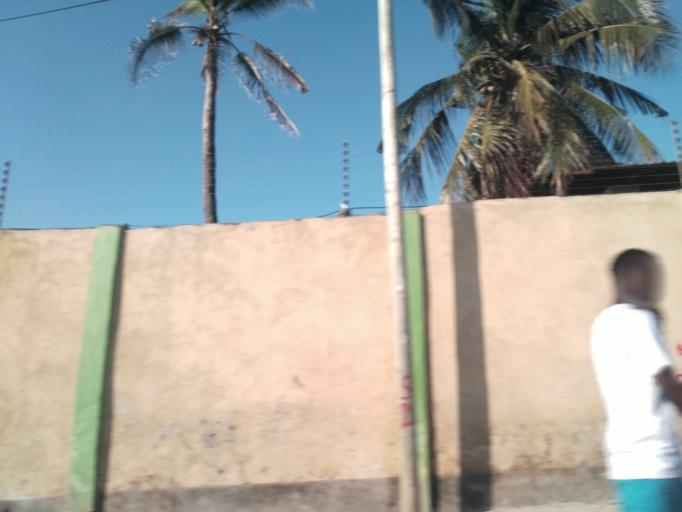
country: TZ
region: Dar es Salaam
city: Magomeni
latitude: -6.7621
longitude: 39.2419
